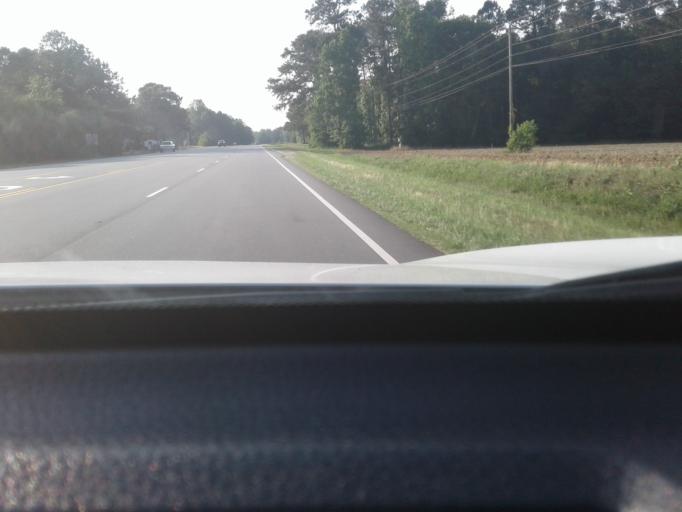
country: US
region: North Carolina
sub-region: Harnett County
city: Buies Creek
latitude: 35.3917
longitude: -78.7282
